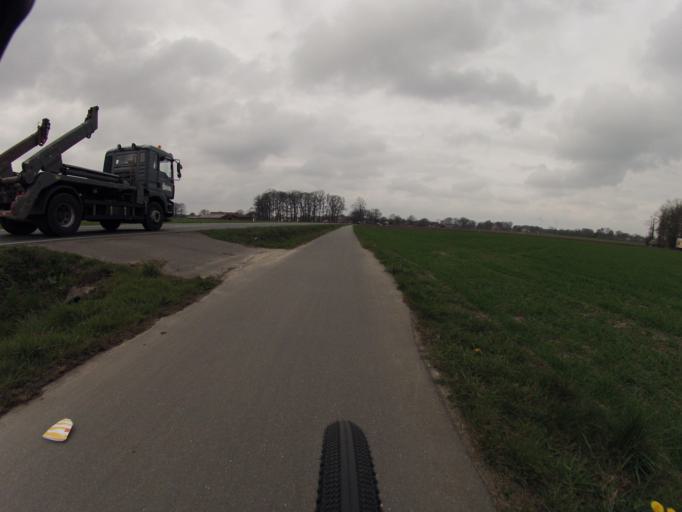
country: DE
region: North Rhine-Westphalia
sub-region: Regierungsbezirk Munster
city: Mettingen
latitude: 52.3258
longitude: 7.7583
